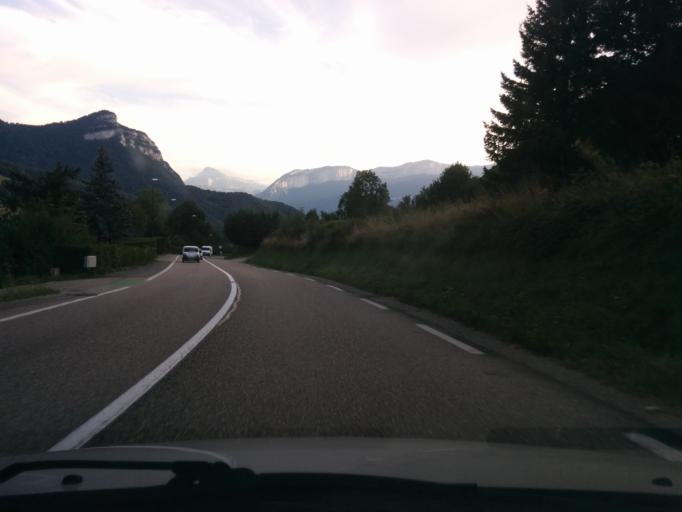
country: FR
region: Rhone-Alpes
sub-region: Departement de l'Isere
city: La Buisse
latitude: 45.3277
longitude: 5.6569
